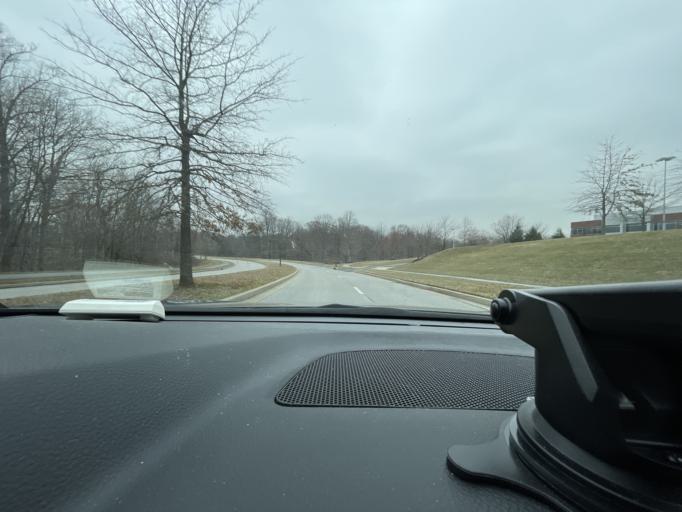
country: US
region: Maryland
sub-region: Anne Arundel County
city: Jessup
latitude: 39.1784
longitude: -76.7994
